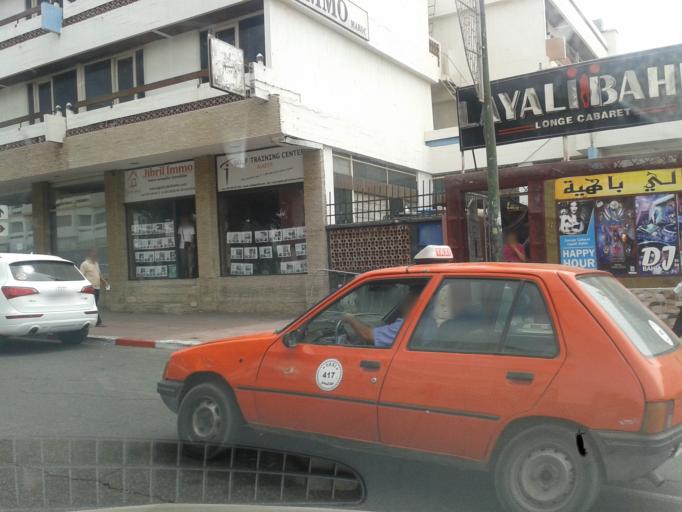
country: MA
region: Souss-Massa-Draa
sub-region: Agadir-Ida-ou-Tnan
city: Agadir
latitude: 30.4229
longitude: -9.6034
